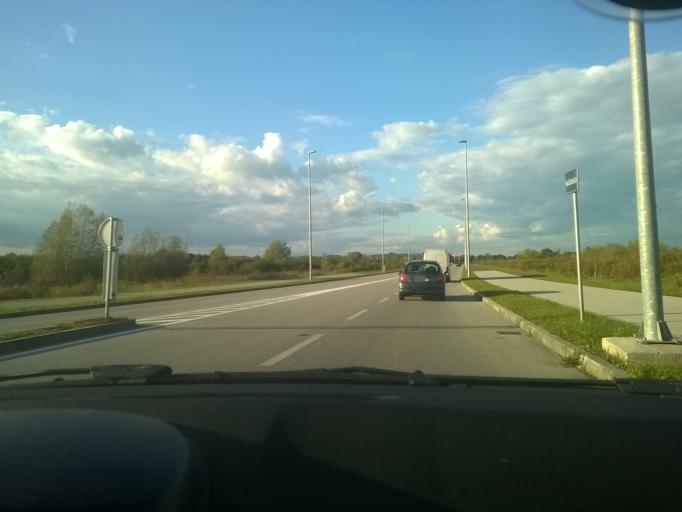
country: HR
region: Zagrebacka
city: Zapresic
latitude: 45.8735
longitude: 15.8252
